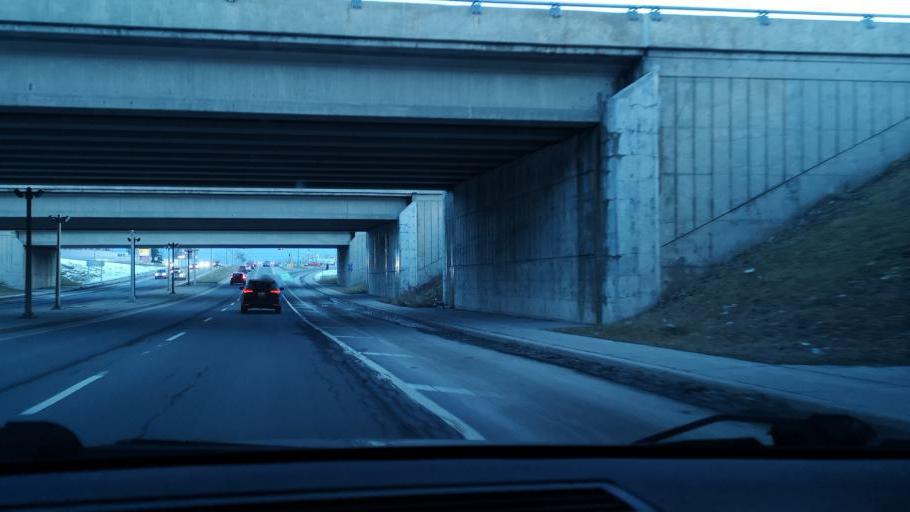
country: CA
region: Quebec
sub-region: Laval
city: Laval
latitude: 45.5681
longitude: -73.7649
